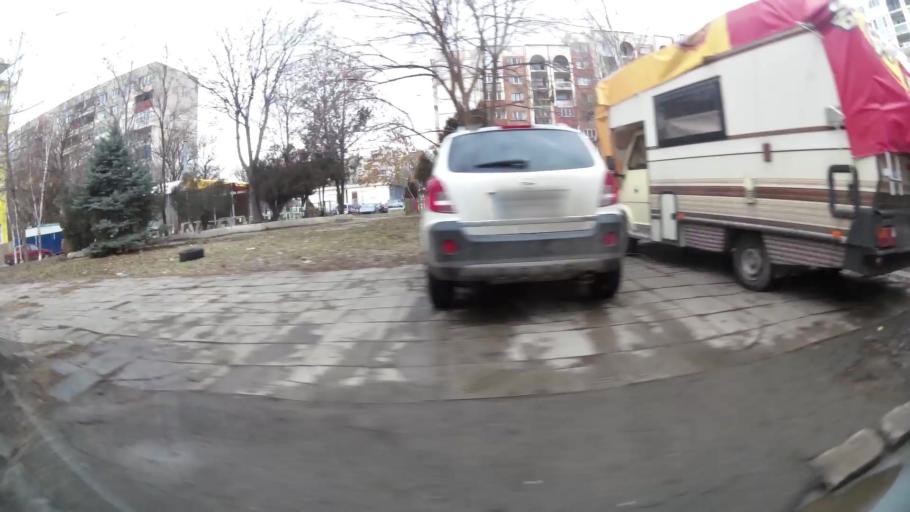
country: BG
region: Sofia-Capital
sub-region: Stolichna Obshtina
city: Sofia
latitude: 42.7268
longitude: 23.3006
